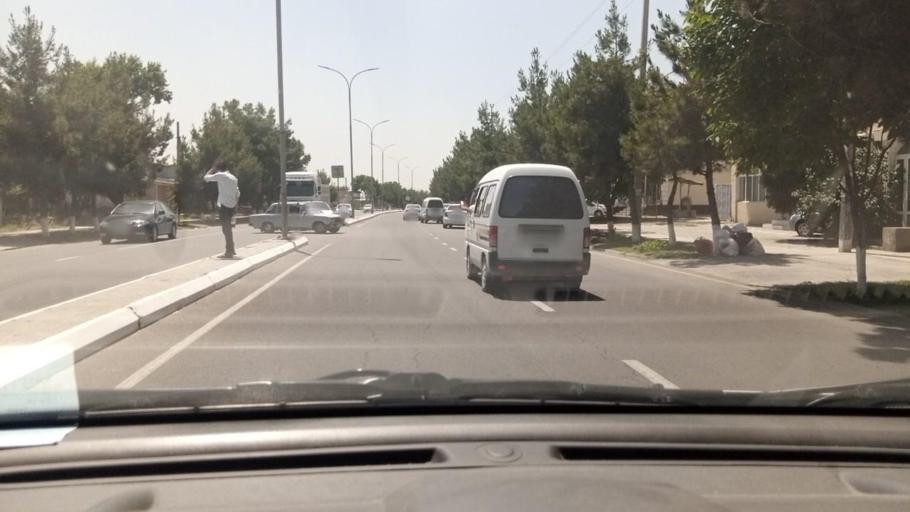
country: UZ
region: Toshkent
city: Urtaowul
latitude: 41.2120
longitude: 69.1715
